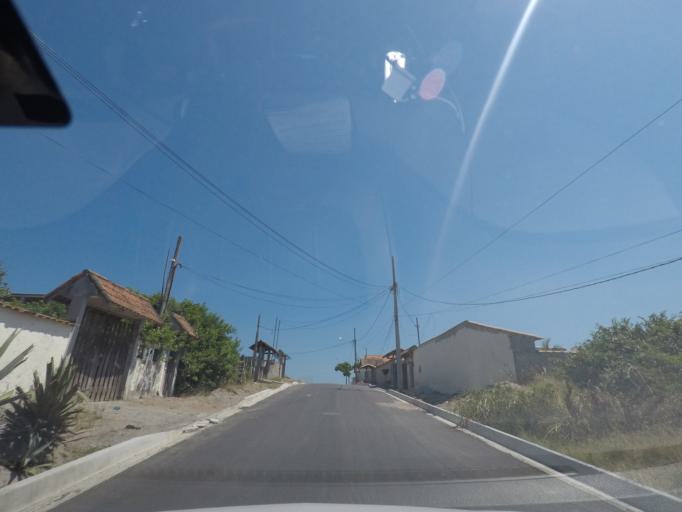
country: BR
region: Rio de Janeiro
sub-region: Marica
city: Marica
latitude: -22.9704
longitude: -42.9046
